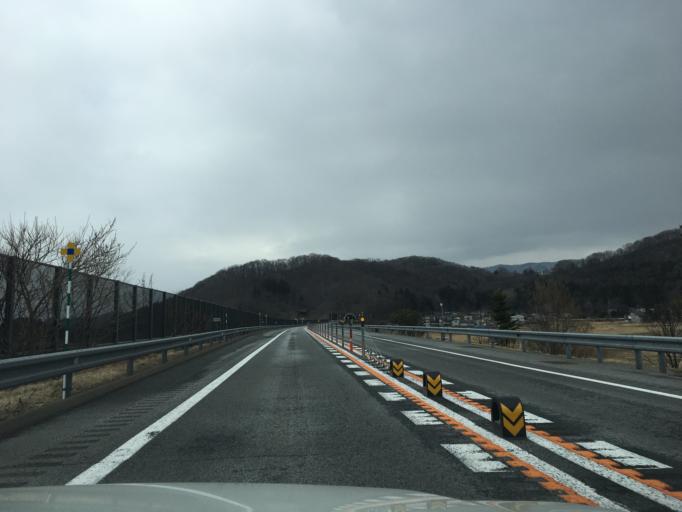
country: JP
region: Aomori
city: Aomori Shi
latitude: 40.8125
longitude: 140.8048
